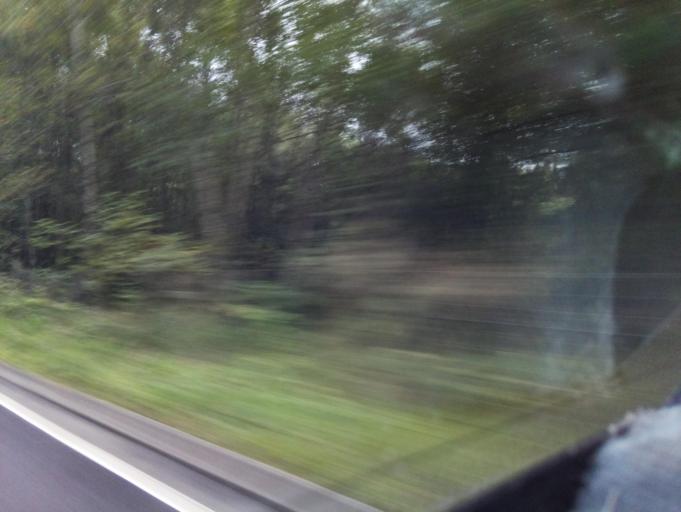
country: GB
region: Scotland
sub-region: Clackmannanshire
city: Dollar
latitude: 56.1794
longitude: -3.6300
